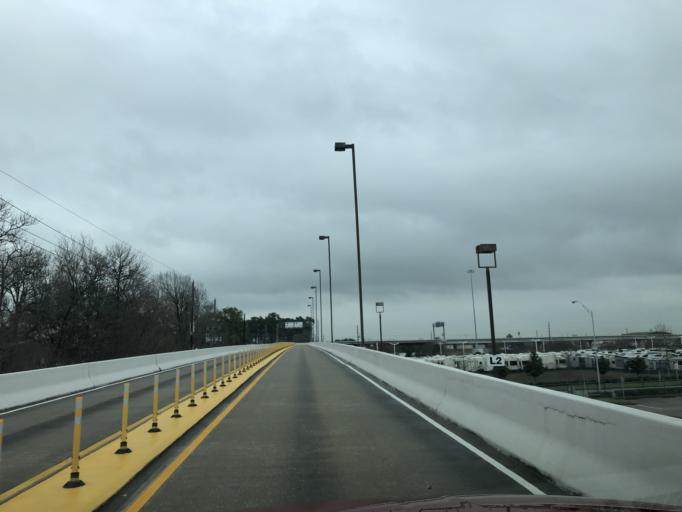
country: US
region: Texas
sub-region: Harris County
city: Aldine
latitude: 29.9740
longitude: -95.4238
